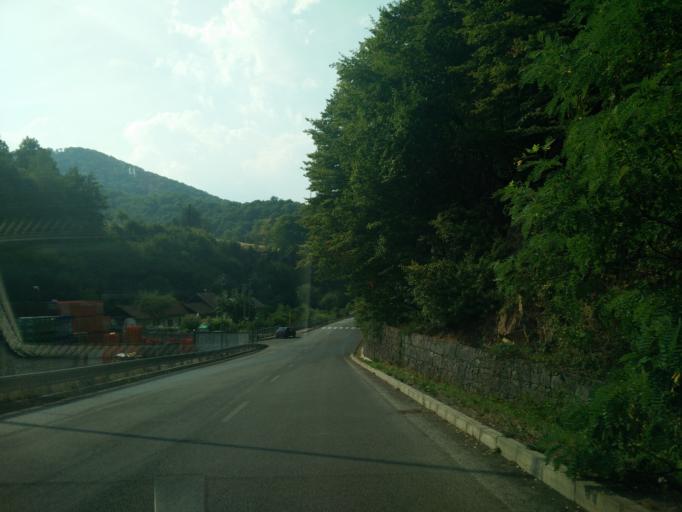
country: SK
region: Banskobystricky
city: Zarnovica
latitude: 48.5081
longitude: 18.7819
